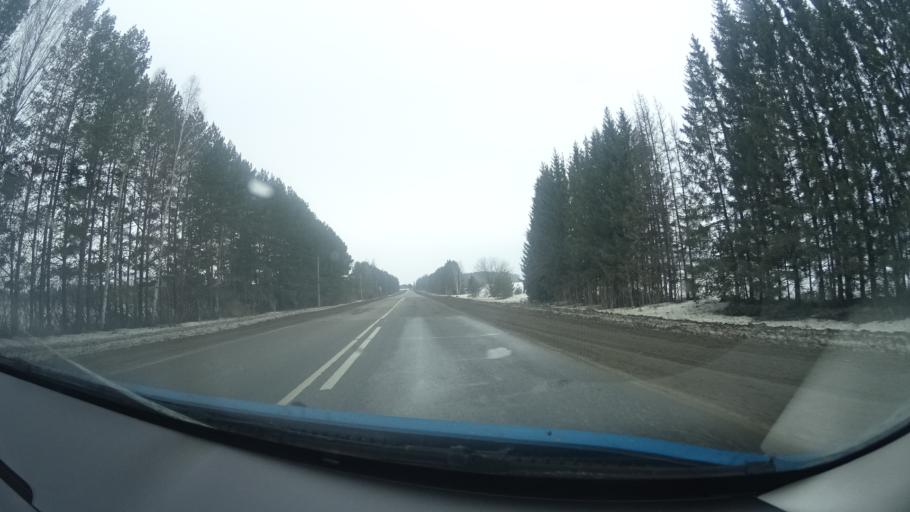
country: RU
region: Perm
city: Osa
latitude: 57.3177
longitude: 55.6217
